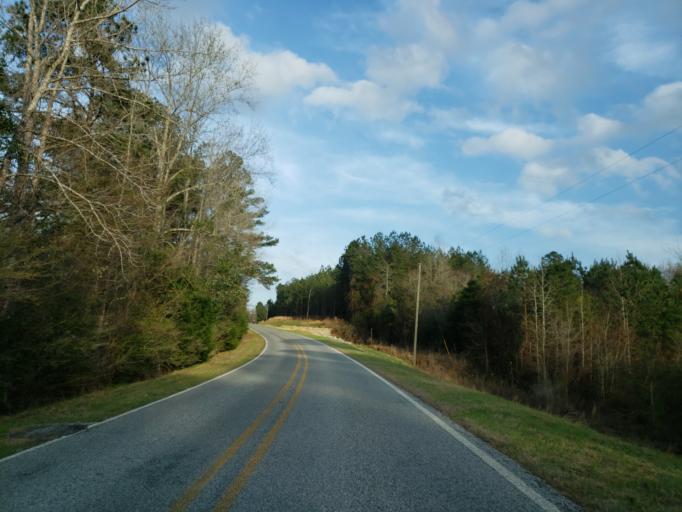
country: US
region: Mississippi
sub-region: Clarke County
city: Stonewall
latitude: 32.1718
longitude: -88.6944
